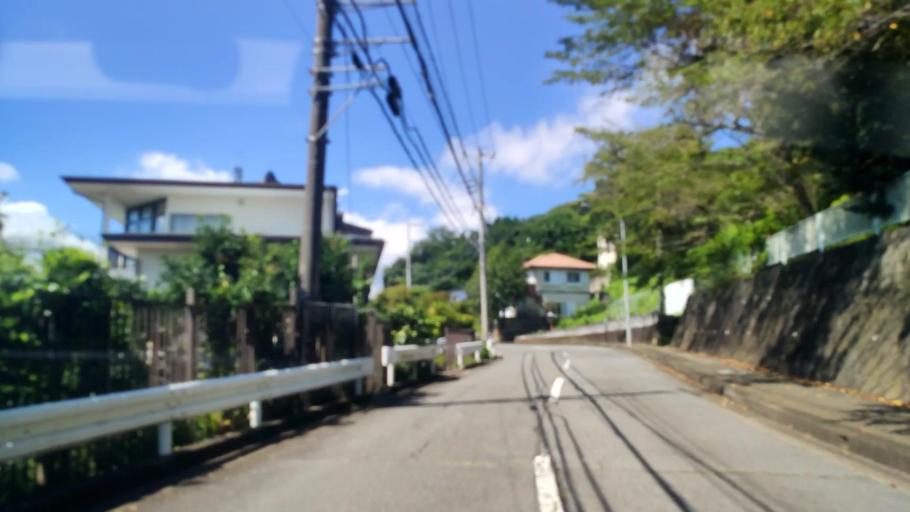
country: JP
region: Kanagawa
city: Odawara
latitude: 35.2522
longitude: 139.1409
